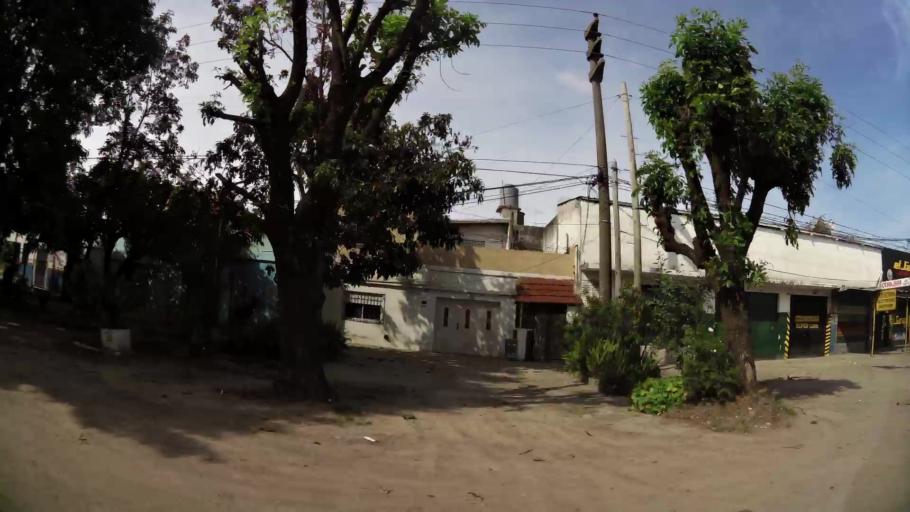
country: AR
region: Buenos Aires
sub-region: Partido de Quilmes
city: Quilmes
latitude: -34.7680
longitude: -58.2469
